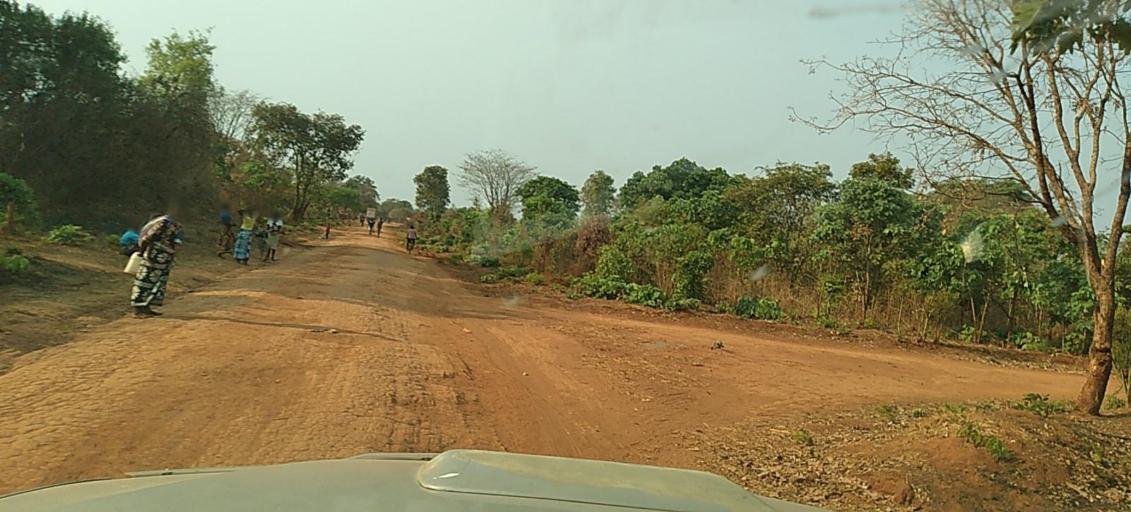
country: ZM
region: North-Western
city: Kasempa
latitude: -13.3049
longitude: 26.5534
